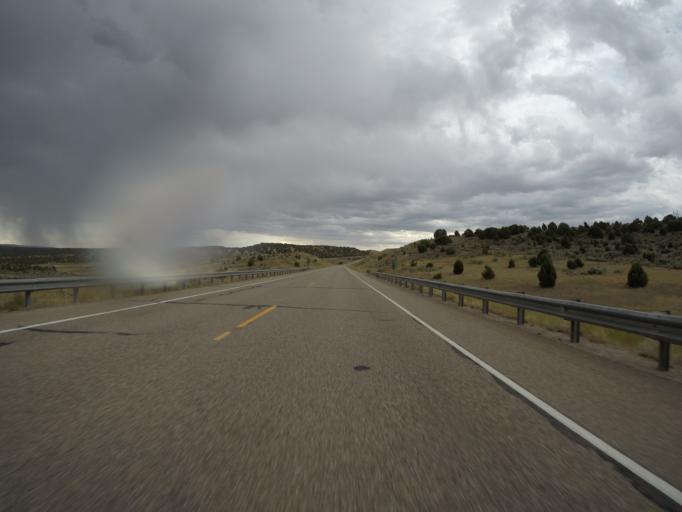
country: US
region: Colorado
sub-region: Rio Blanco County
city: Rangely
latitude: 40.3659
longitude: -108.4133
